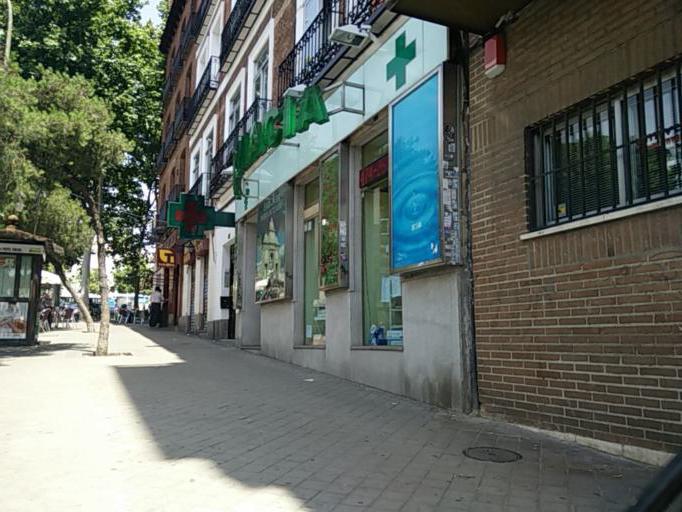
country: ES
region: Madrid
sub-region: Provincia de Madrid
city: Madrid
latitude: 40.4058
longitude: -3.7118
